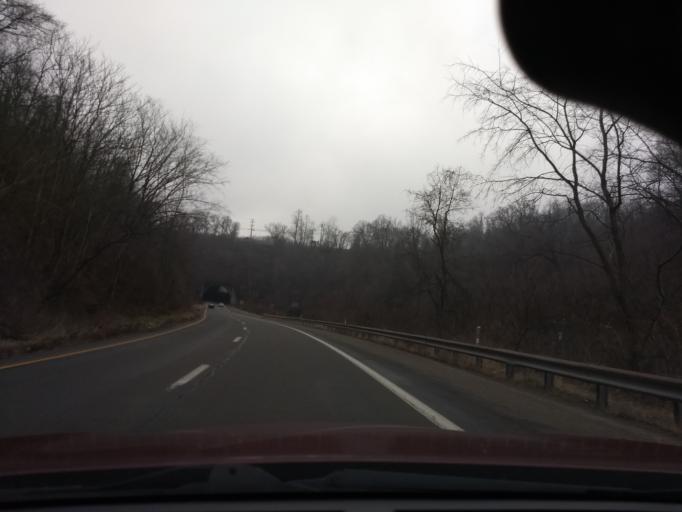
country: US
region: Pennsylvania
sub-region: Allegheny County
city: East Pittsburgh
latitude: 40.3908
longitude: -79.8285
